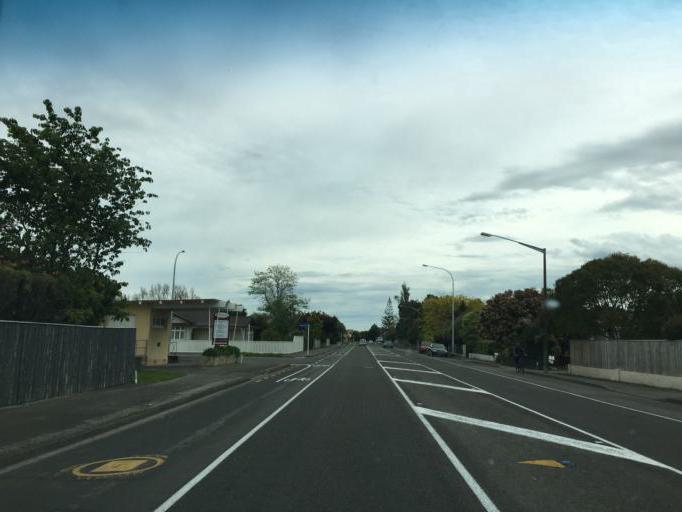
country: NZ
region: Manawatu-Wanganui
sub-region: Palmerston North City
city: Palmerston North
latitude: -40.3554
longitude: 175.5940
